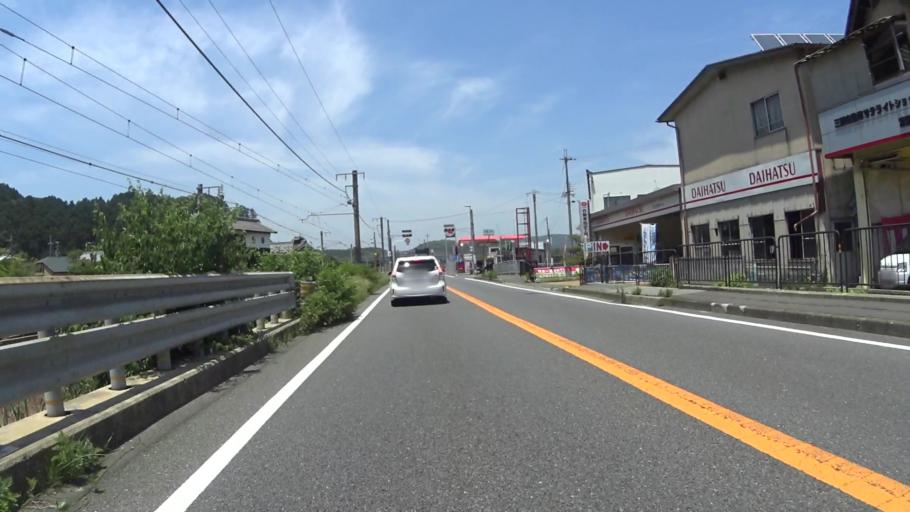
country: JP
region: Kyoto
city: Kameoka
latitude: 35.0721
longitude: 135.5277
